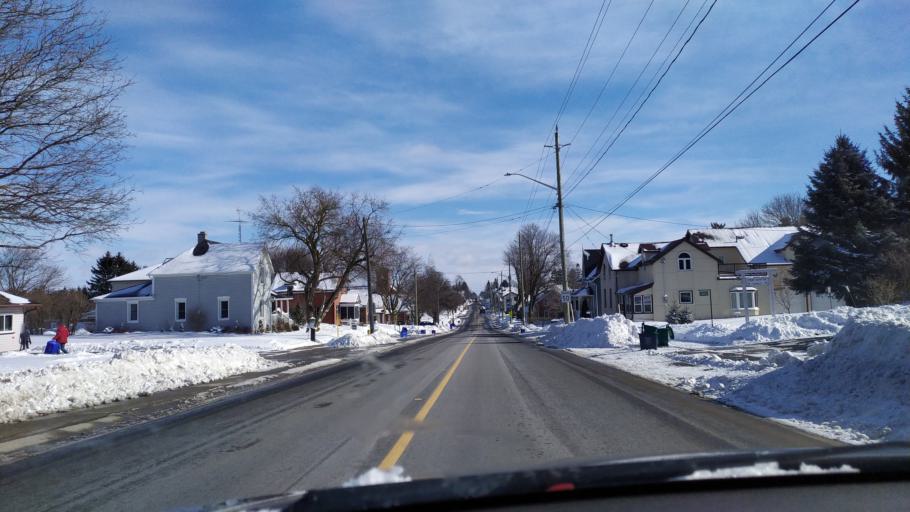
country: CA
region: Ontario
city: Waterloo
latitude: 43.5235
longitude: -80.6576
